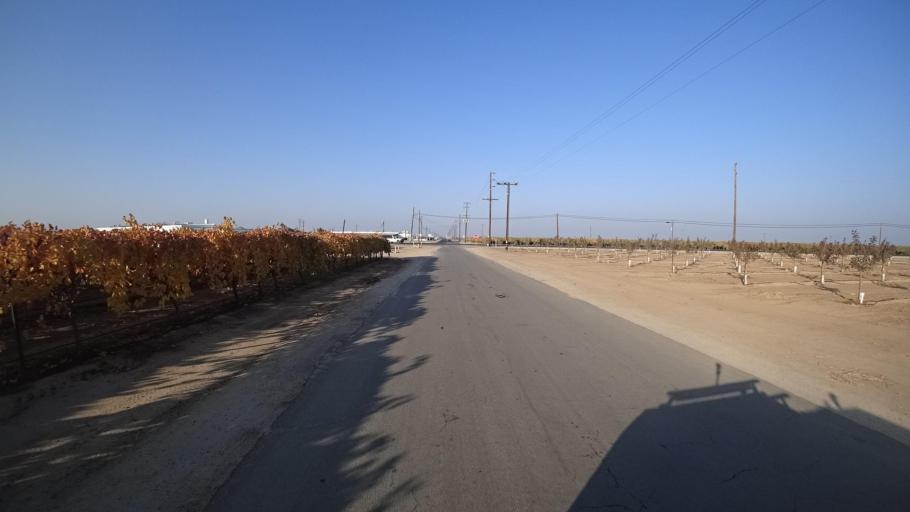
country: US
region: California
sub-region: Tulare County
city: Richgrove
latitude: 35.7761
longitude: -119.1226
